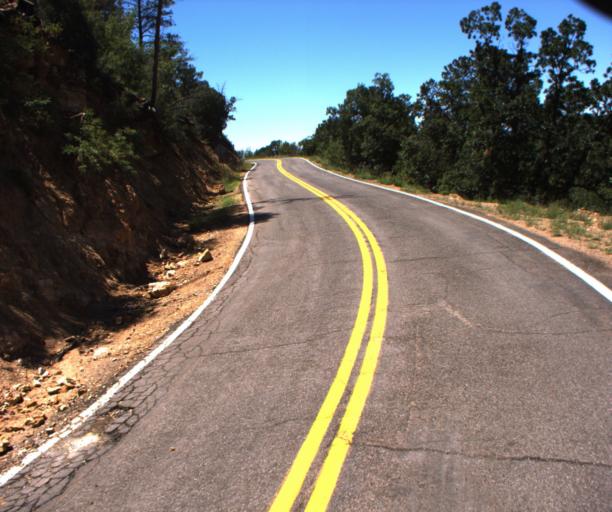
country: US
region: Arizona
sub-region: Greenlee County
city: Morenci
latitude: 33.2029
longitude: -109.3801
